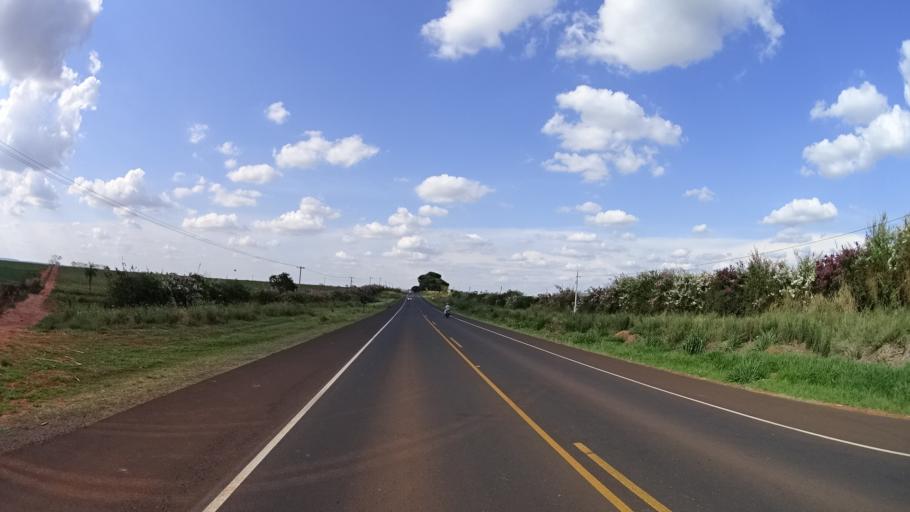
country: BR
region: Sao Paulo
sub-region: Urupes
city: Urupes
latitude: -21.0338
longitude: -49.2392
